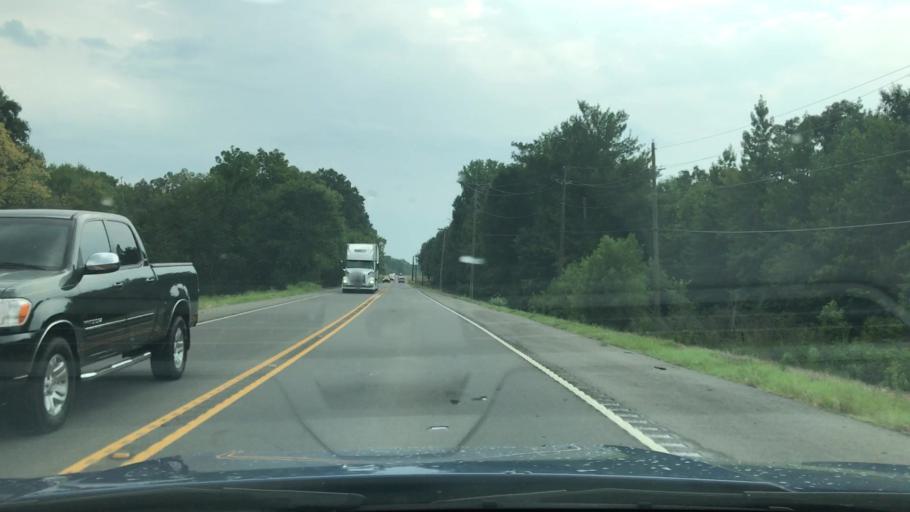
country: US
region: Texas
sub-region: Harrison County
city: Waskom
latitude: 32.4581
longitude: -94.0177
